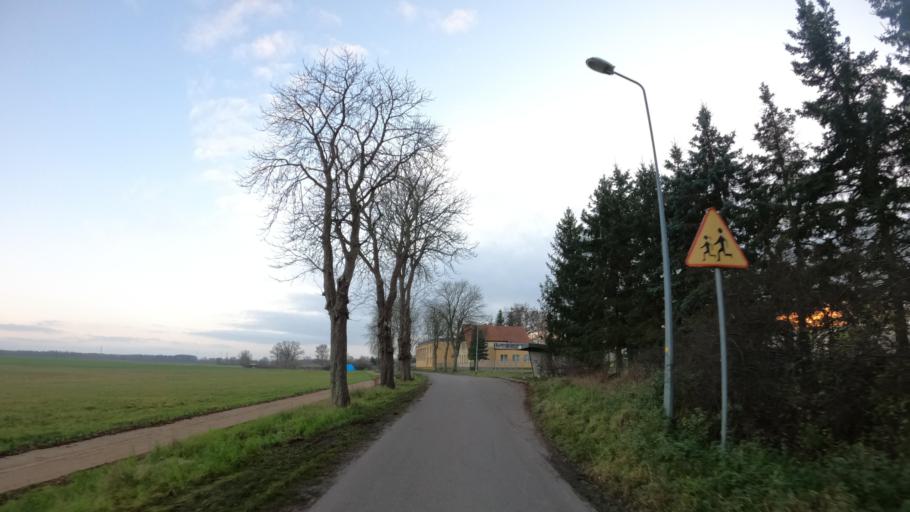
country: PL
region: West Pomeranian Voivodeship
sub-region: Powiat bialogardzki
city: Karlino
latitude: 54.0820
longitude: 15.8813
